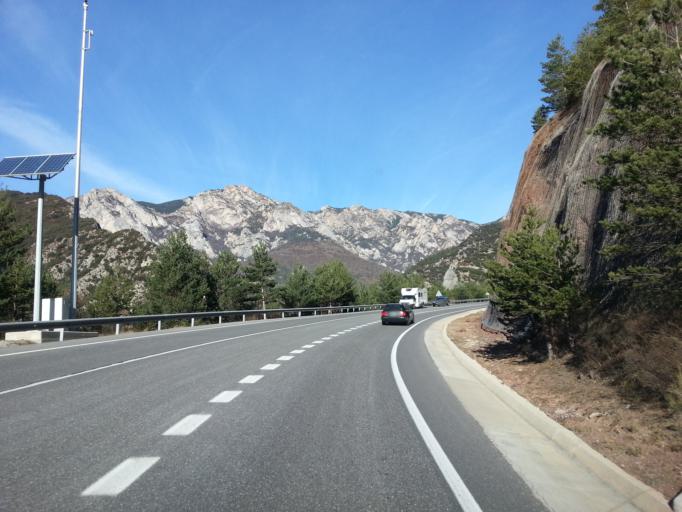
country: ES
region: Catalonia
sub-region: Provincia de Barcelona
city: Baga
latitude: 42.2660
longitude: 1.8521
